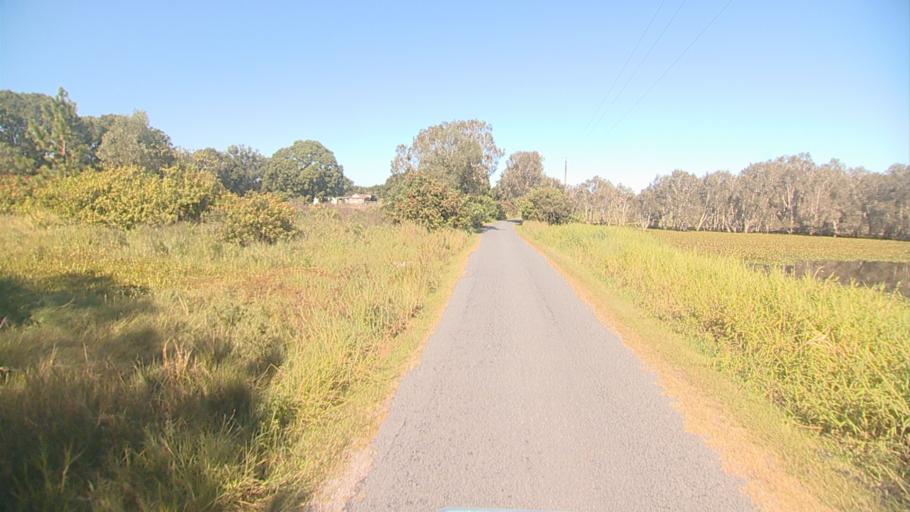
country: AU
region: Queensland
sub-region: Gold Coast
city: Yatala
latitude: -27.6852
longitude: 153.2247
